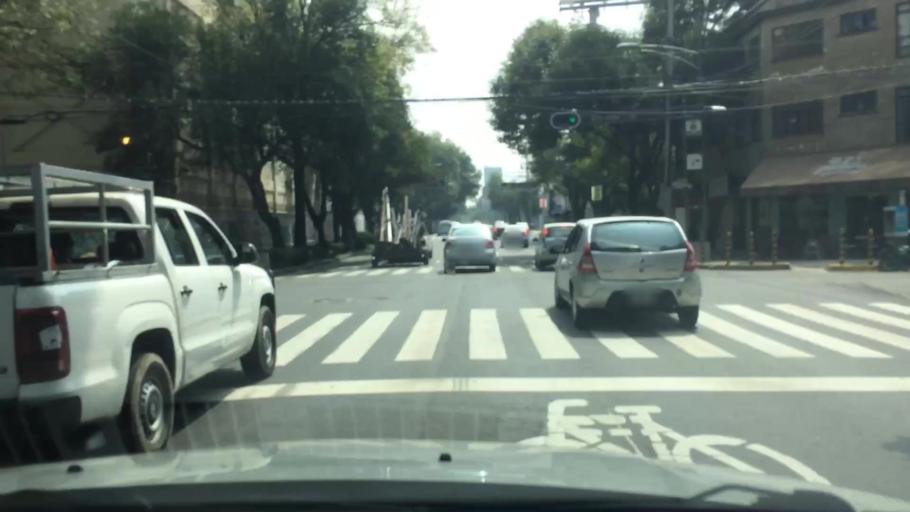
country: MX
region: Mexico City
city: Colonia del Valle
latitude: 19.3817
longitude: -99.1609
